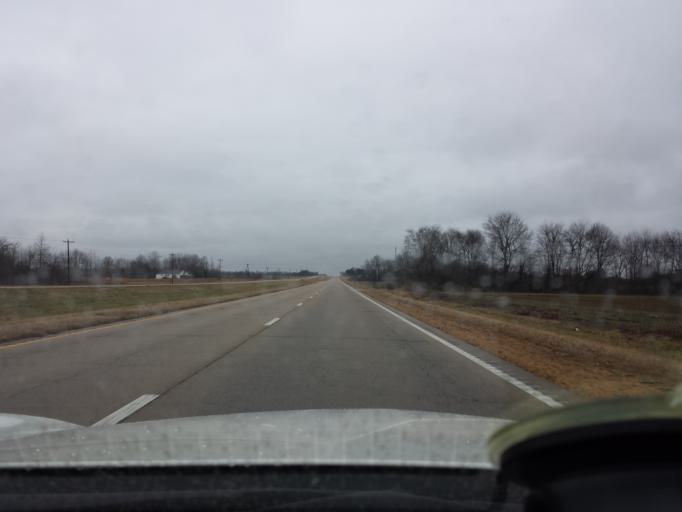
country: US
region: Mississippi
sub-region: Chickasaw County
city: Okolona
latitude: 33.8831
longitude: -88.7246
